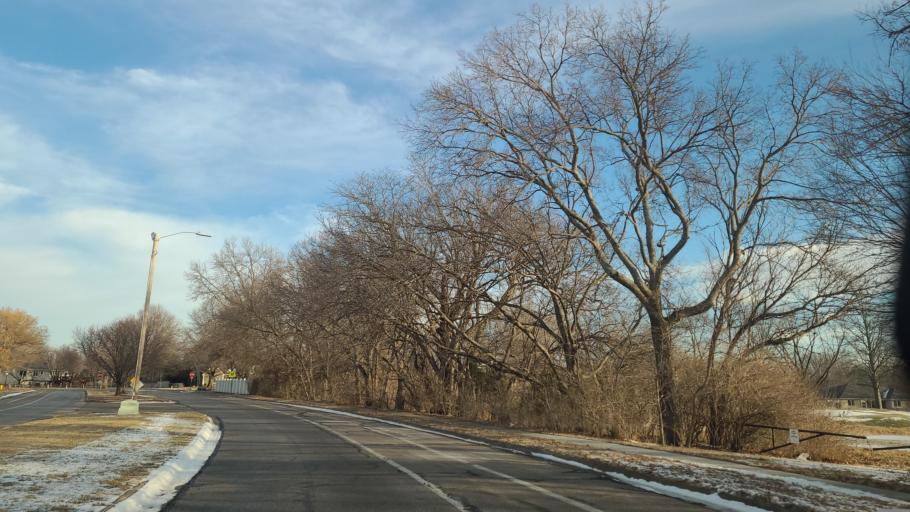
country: US
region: Kansas
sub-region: Douglas County
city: Lawrence
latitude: 38.9824
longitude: -95.2700
